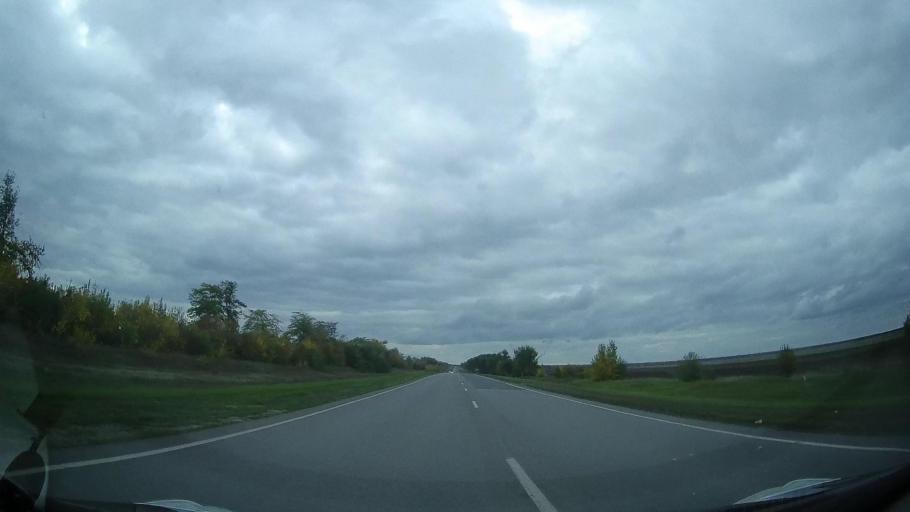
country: RU
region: Rostov
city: Yegorlykskaya
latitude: 46.5483
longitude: 40.7425
